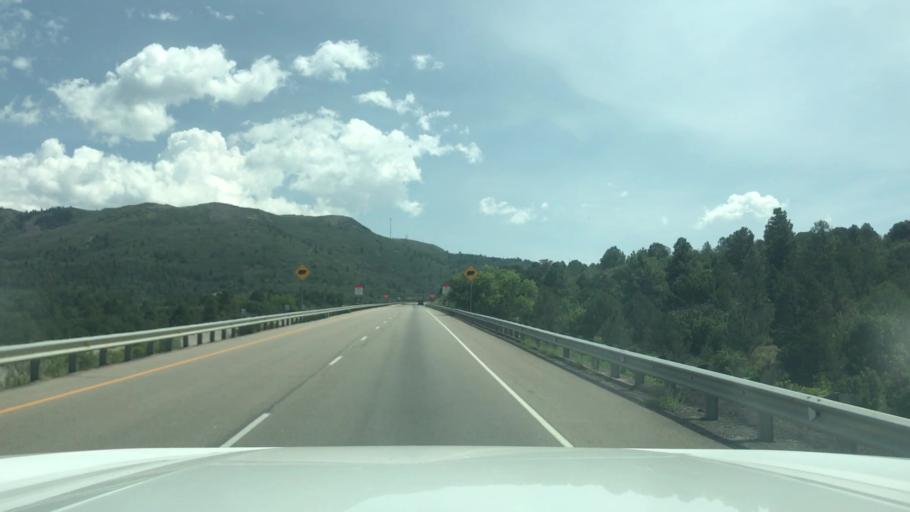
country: US
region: New Mexico
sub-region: Colfax County
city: Raton
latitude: 37.0142
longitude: -104.4823
